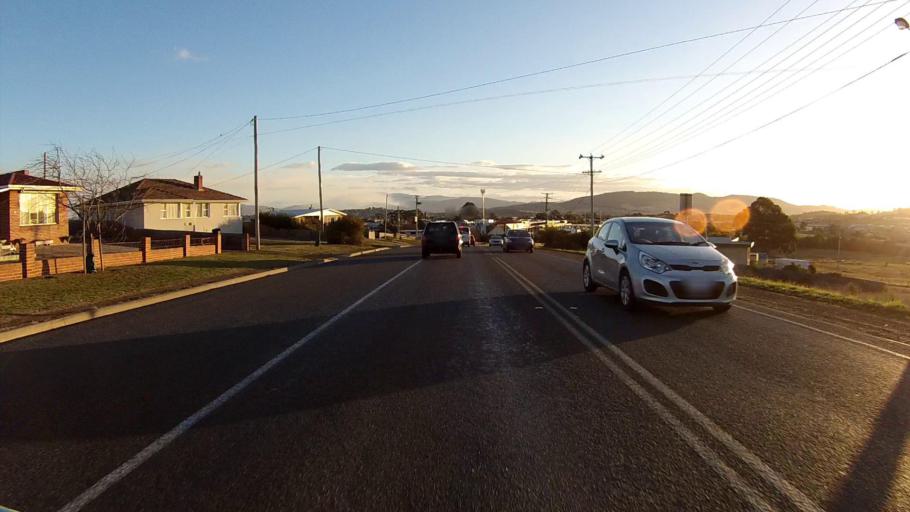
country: AU
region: Tasmania
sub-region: Sorell
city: Sorell
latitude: -42.7821
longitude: 147.5710
